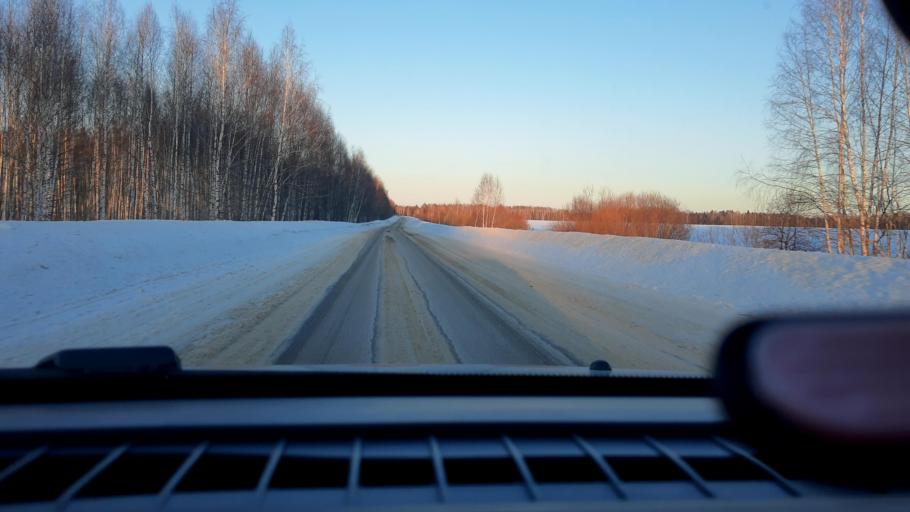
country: RU
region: Nizjnij Novgorod
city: Pervoye Maya
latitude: 56.1565
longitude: 44.8886
